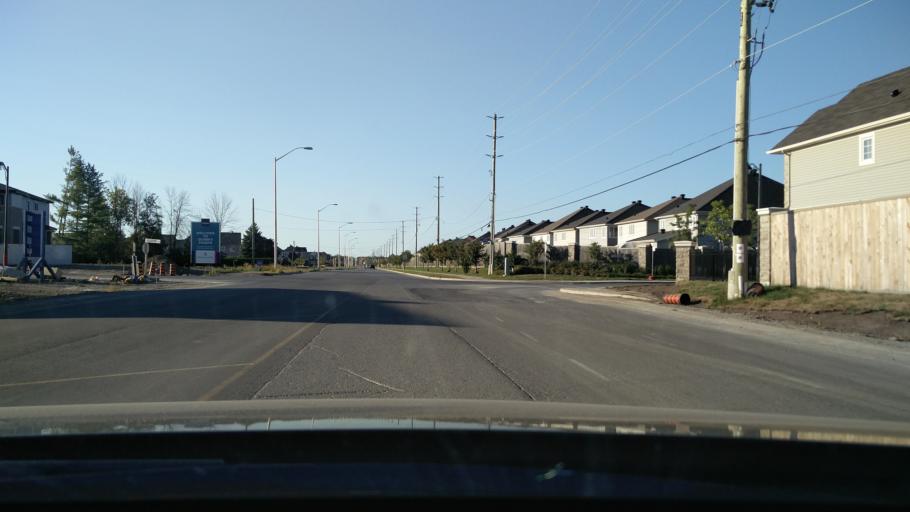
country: CA
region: Ontario
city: Bells Corners
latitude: 45.2418
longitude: -75.7292
